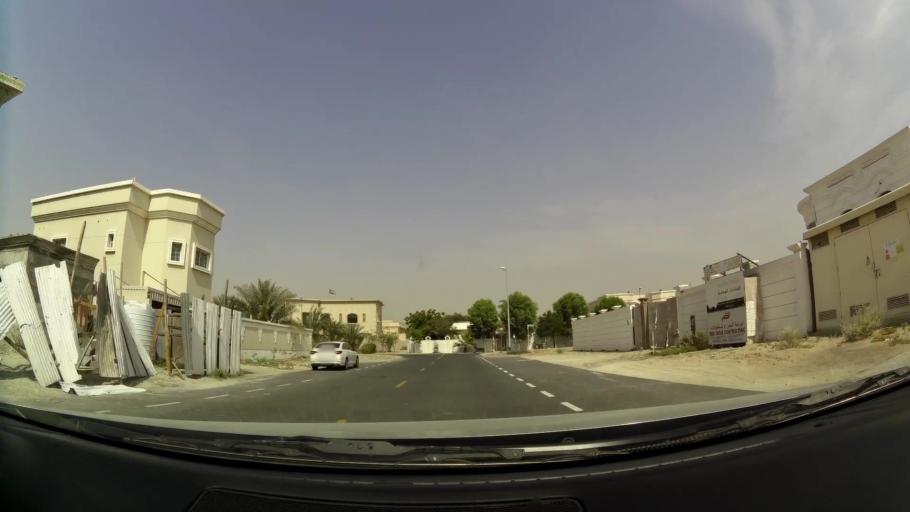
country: AE
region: Ash Shariqah
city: Sharjah
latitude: 25.2467
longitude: 55.4384
